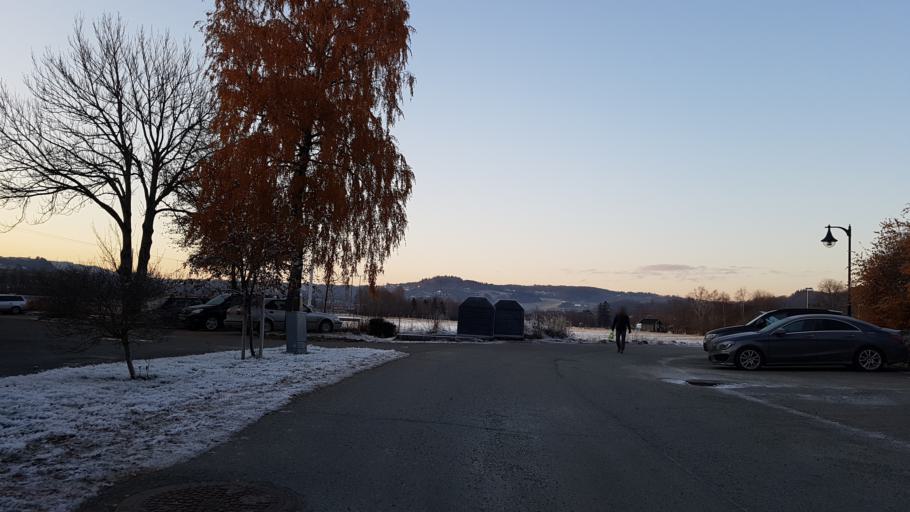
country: NO
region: Sor-Trondelag
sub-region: Melhus
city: Melhus
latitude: 63.2747
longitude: 10.2917
